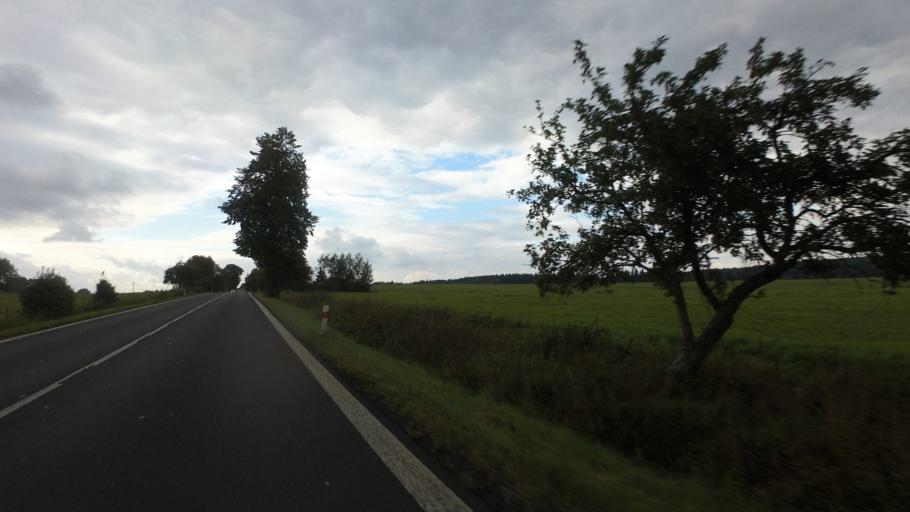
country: CZ
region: Ustecky
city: Stare Krecany
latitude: 50.9687
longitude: 14.5223
